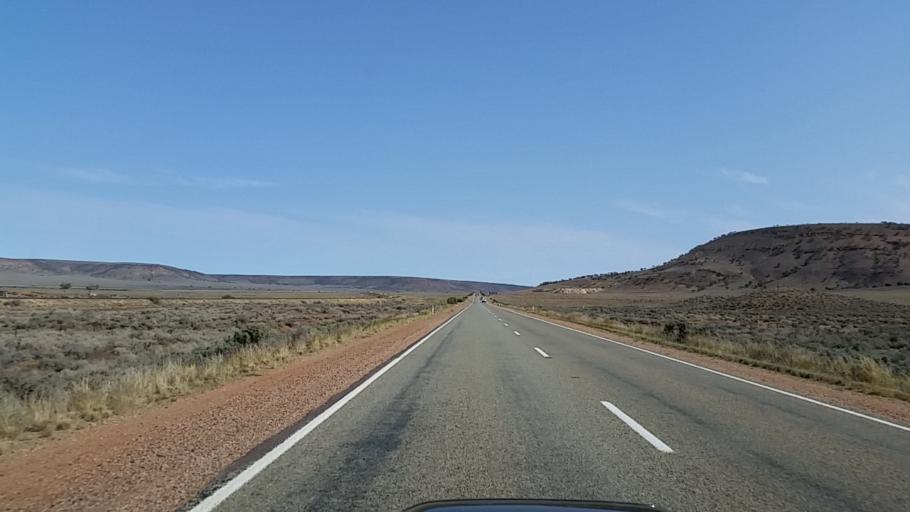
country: AU
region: South Australia
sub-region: Port Augusta
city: Port Augusta West
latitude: -32.5597
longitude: 137.6295
